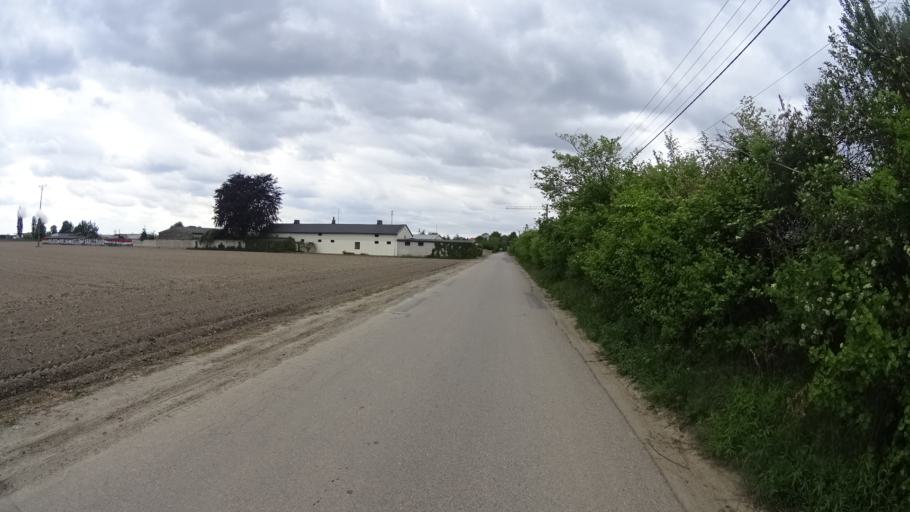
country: PL
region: Masovian Voivodeship
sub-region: Powiat pruszkowski
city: Piastow
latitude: 52.2103
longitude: 20.8527
